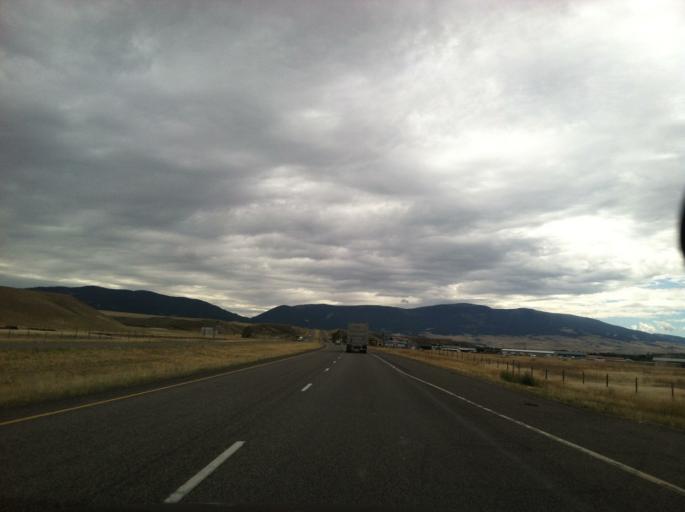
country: US
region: Montana
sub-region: Park County
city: Livingston
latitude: 45.6843
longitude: -110.5058
